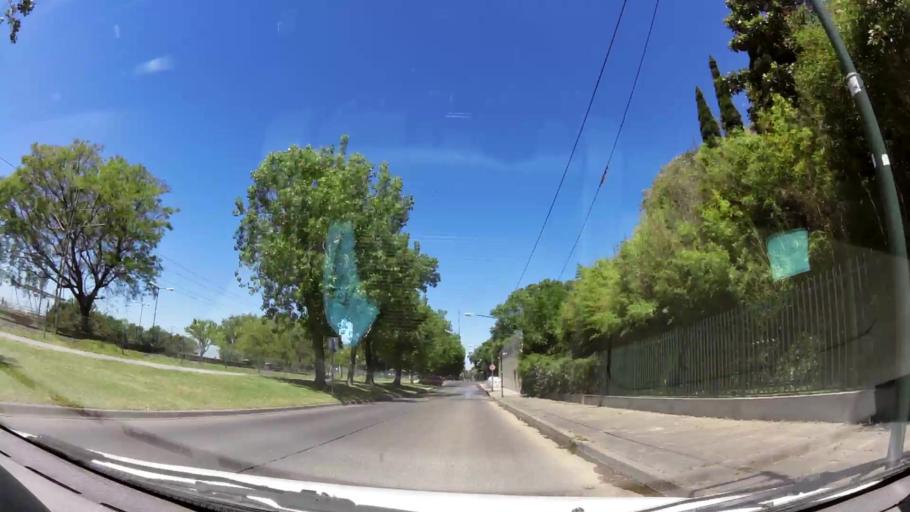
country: AR
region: Buenos Aires
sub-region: Partido de Vicente Lopez
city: Olivos
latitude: -34.4873
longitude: -58.4815
